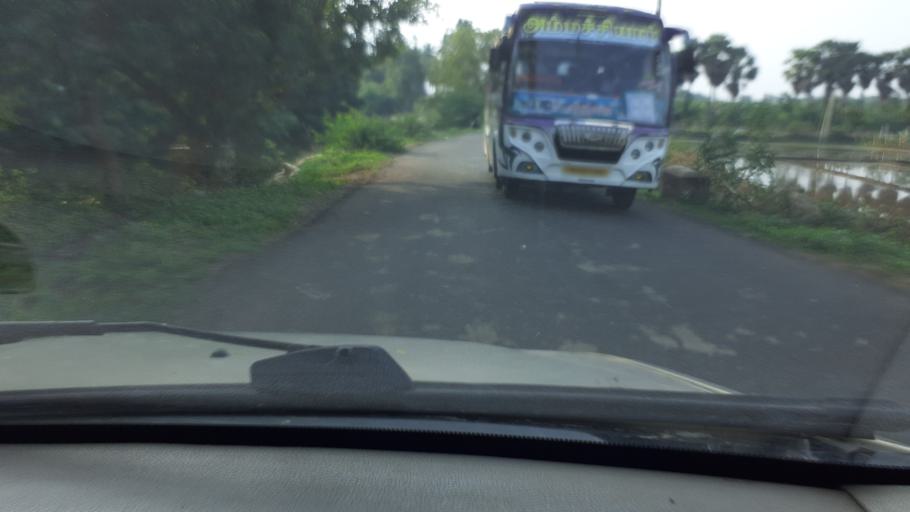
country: IN
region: Tamil Nadu
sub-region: Thoothukkudi
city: Alwar Tirunagari
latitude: 8.5951
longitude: 77.9735
